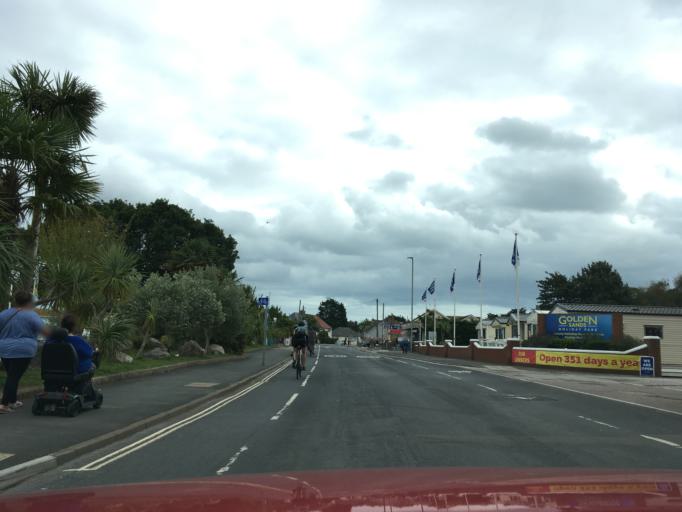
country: GB
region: England
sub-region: Devon
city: Dawlish
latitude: 50.5997
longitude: -3.4472
